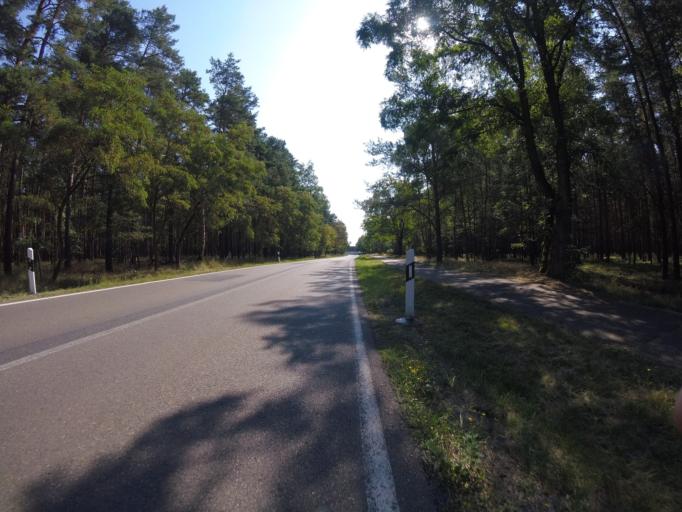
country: DE
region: Brandenburg
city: Jacobsdorf
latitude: 52.2700
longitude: 14.3464
